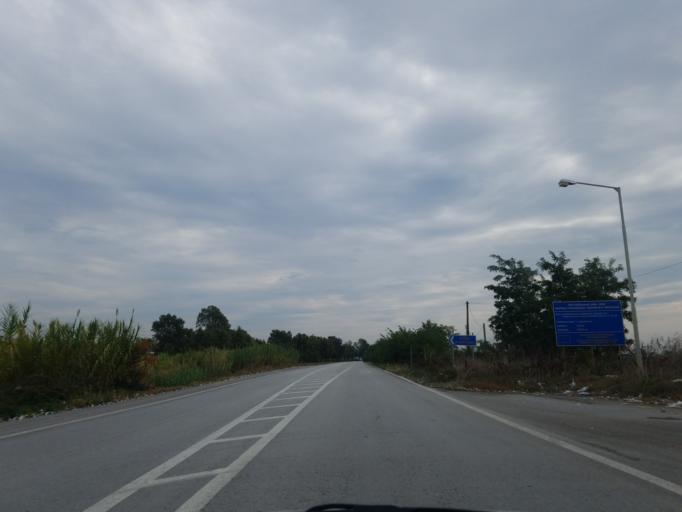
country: GR
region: Thessaly
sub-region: Nomos Kardhitsas
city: Sofades
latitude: 39.3237
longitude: 22.1049
